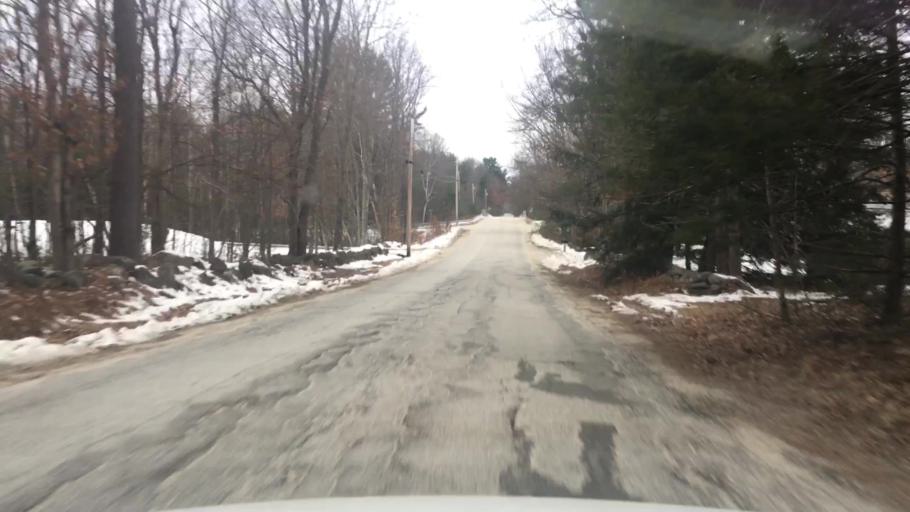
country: US
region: New Hampshire
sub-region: Merrimack County
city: Hopkinton
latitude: 43.1812
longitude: -71.6746
